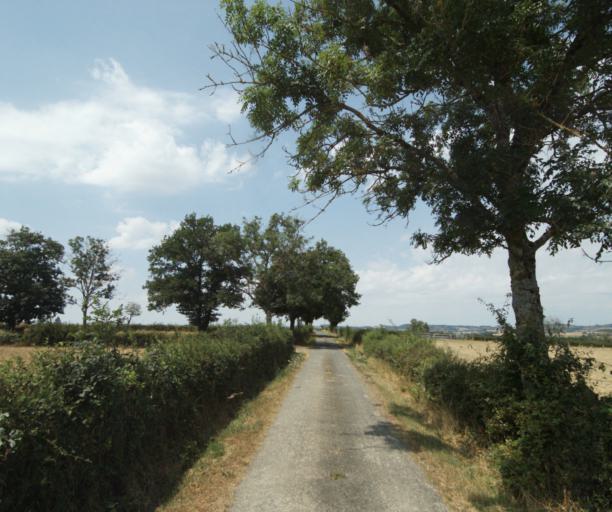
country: FR
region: Bourgogne
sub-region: Departement de Saone-et-Loire
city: Gueugnon
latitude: 46.6074
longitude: 4.0157
